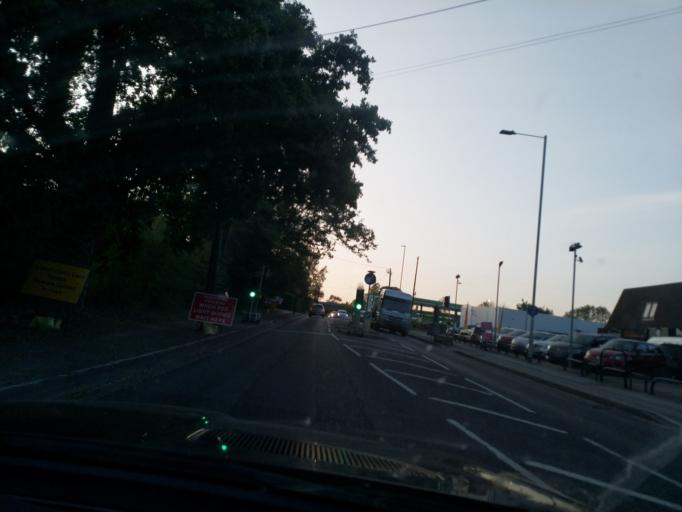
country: GB
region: England
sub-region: Kent
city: Leysdown-on-Sea
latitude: 51.4235
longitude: 0.8659
